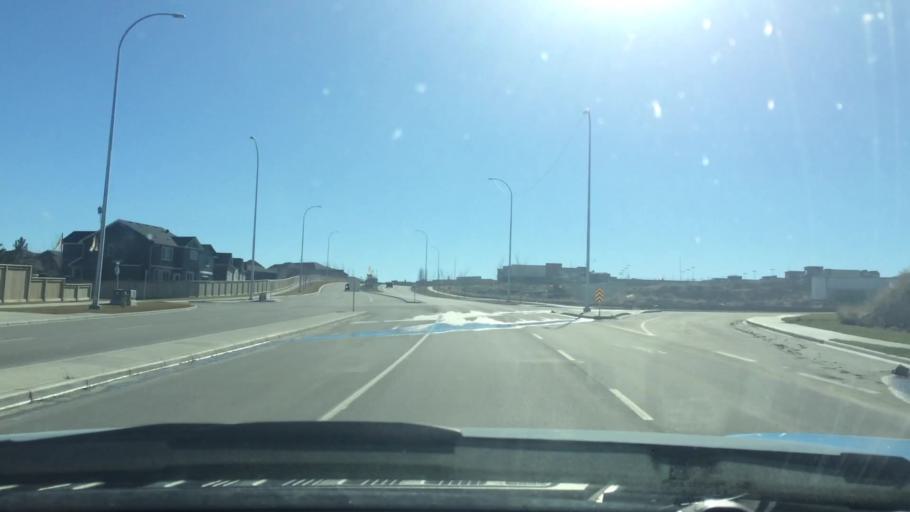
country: CA
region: Alberta
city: Calgary
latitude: 51.1660
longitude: -114.1606
